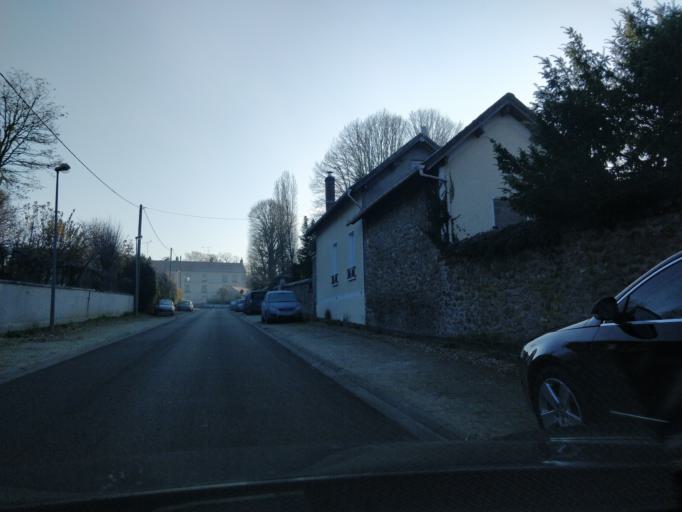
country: FR
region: Ile-de-France
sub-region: Departement de l'Essonne
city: Briis-sous-Forges
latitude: 48.6239
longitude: 2.1203
